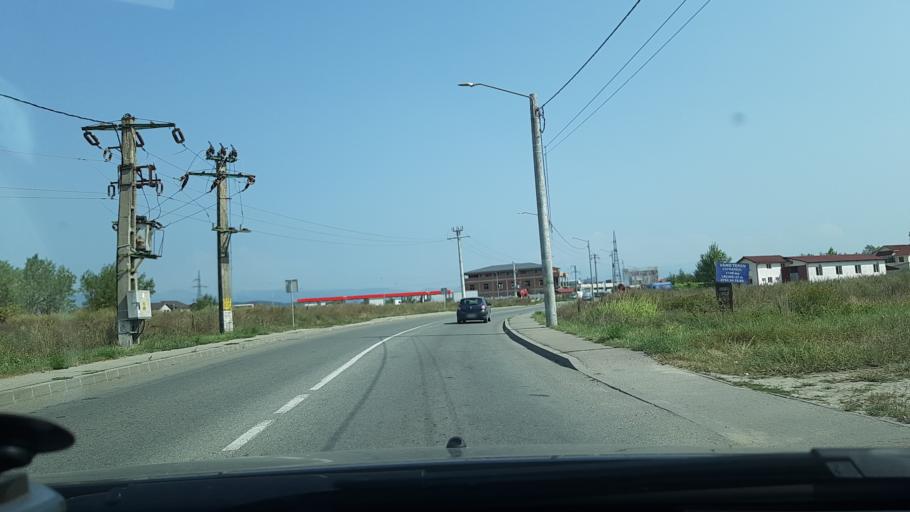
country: RO
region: Gorj
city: Targu Jiu
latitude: 45.0184
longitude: 23.2604
